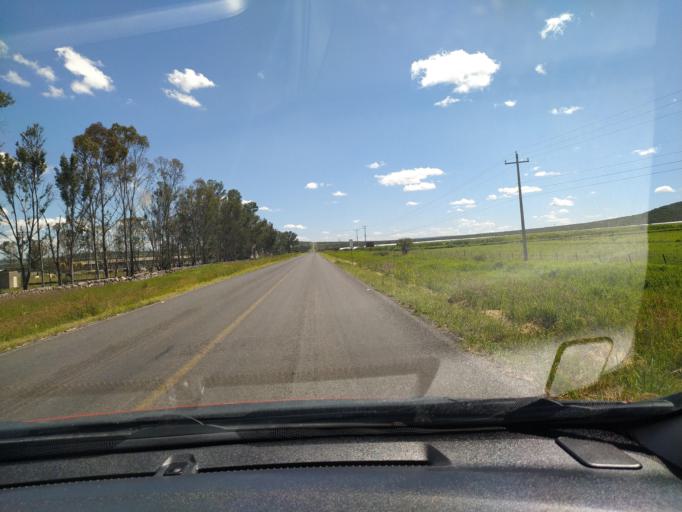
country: MX
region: Jalisco
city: San Miguel el Alto
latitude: 21.0176
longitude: -102.4663
